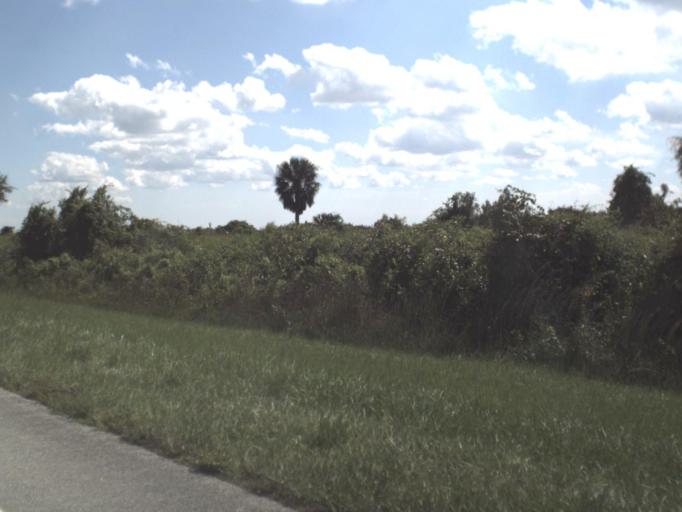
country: US
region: Florida
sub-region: Highlands County
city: Lake Placid
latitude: 27.3919
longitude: -81.1480
